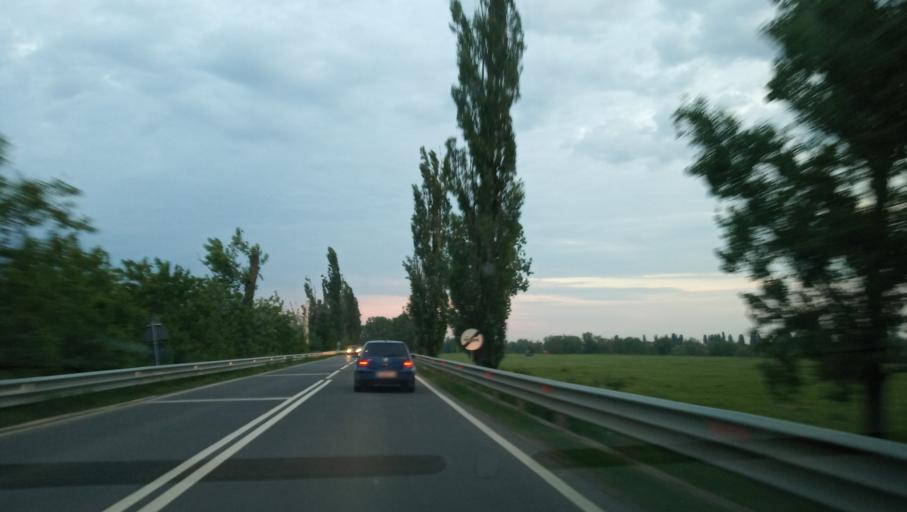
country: RO
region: Timis
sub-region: Comuna Sag
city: Sag
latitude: 45.6398
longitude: 21.1796
